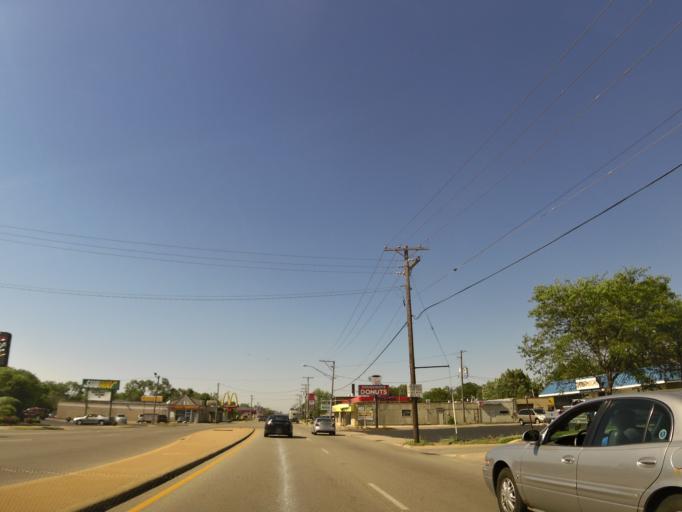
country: US
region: Illinois
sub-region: Winnebago County
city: Rockford
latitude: 42.2239
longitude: -89.0722
